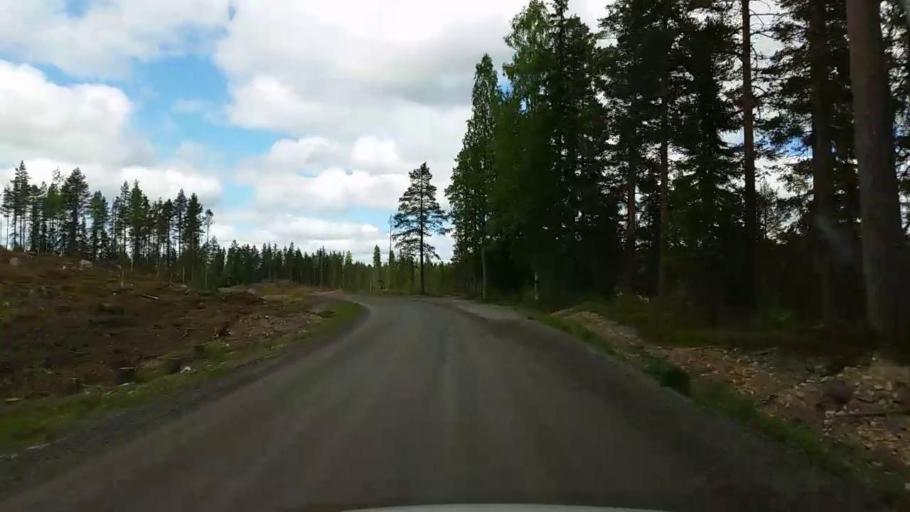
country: SE
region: Gaevleborg
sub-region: Bollnas Kommun
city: Vittsjo
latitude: 61.1669
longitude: 16.1569
